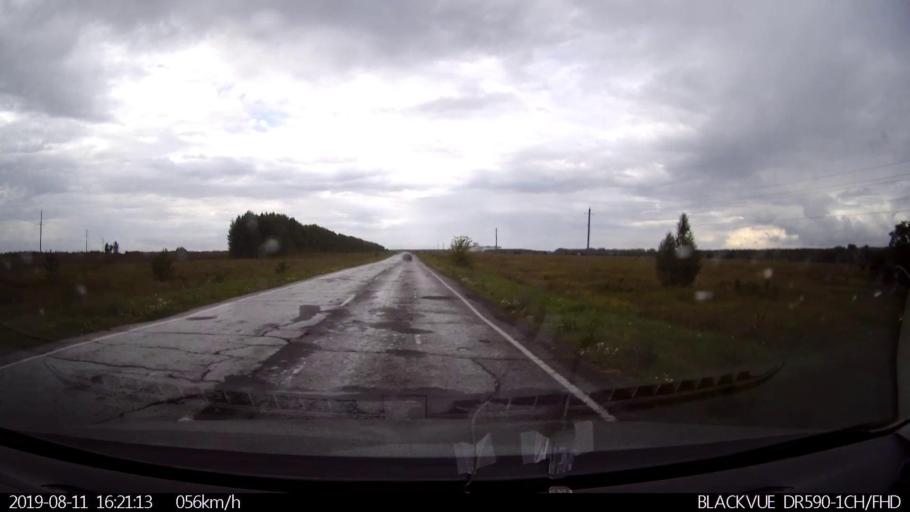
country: RU
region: Ulyanovsk
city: Mayna
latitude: 54.0782
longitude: 47.5990
